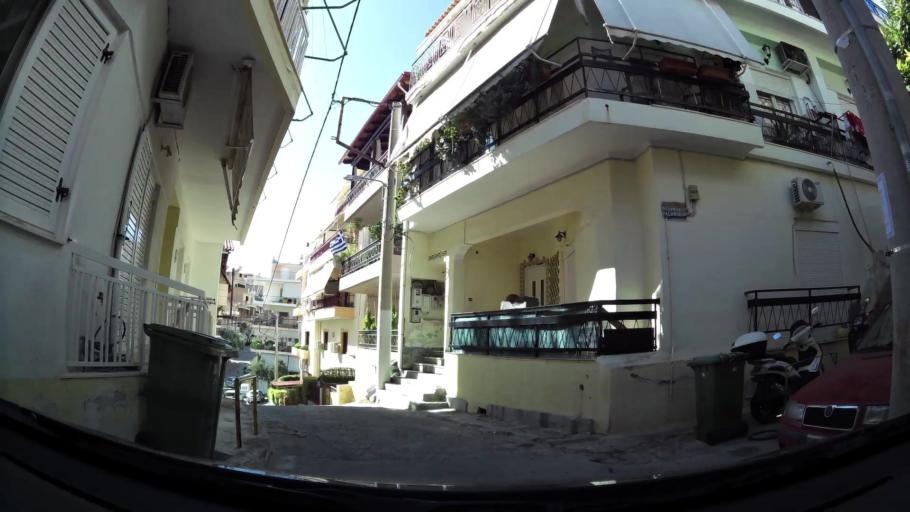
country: GR
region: Attica
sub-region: Nomos Piraios
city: Perama
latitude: 37.9696
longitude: 23.5654
